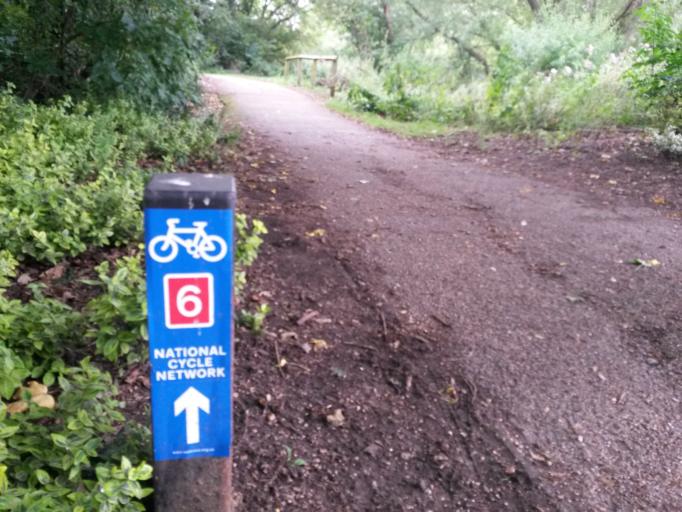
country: GB
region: England
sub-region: Milton Keynes
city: Simpson
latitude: 52.0158
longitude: -0.7109
